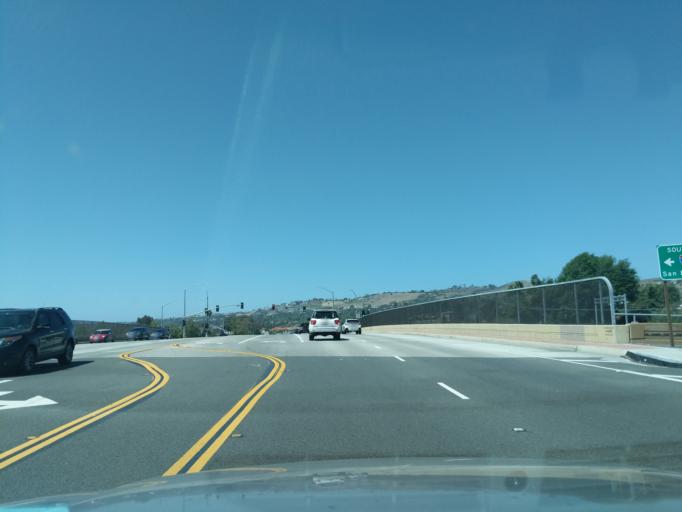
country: US
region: California
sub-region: Orange County
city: San Juan Capistrano
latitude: 33.5027
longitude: -117.6580
